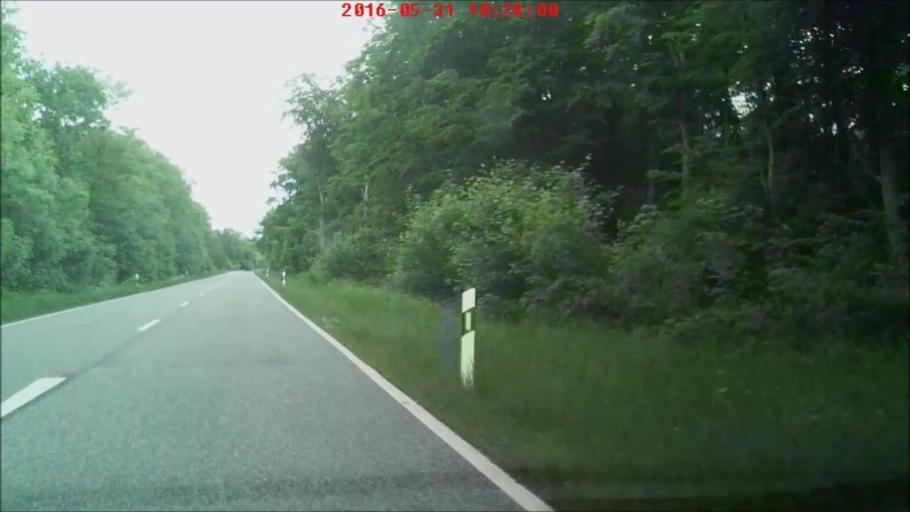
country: DE
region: Thuringia
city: Bad Frankenhausen
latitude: 51.4055
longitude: 11.0868
